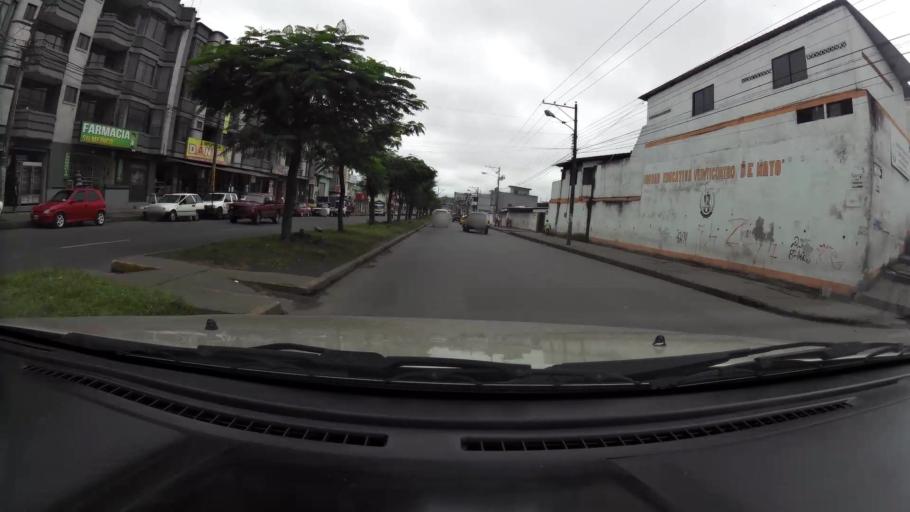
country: EC
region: Santo Domingo de los Tsachilas
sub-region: Canton Santo Domingo de los Colorados
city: Santo Domingo de los Colorados
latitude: -0.2502
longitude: -79.1753
